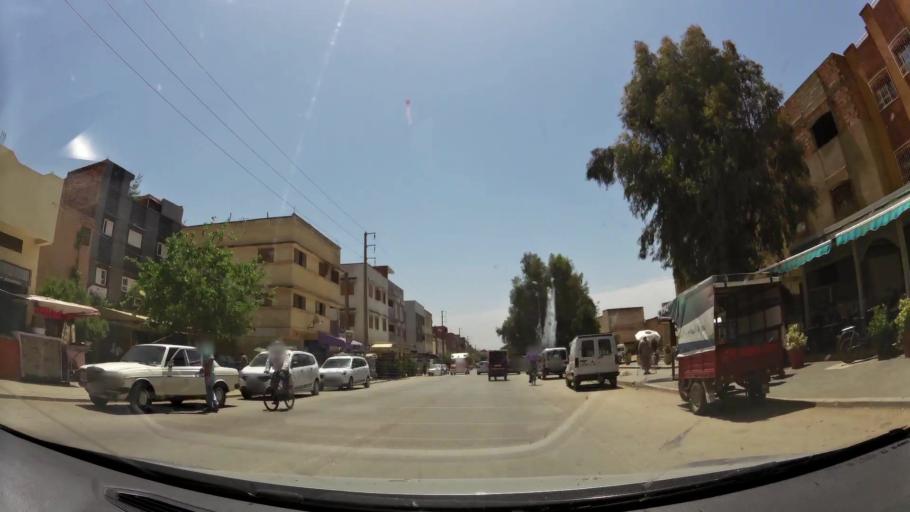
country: MA
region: Rabat-Sale-Zemmour-Zaer
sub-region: Khemisset
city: Khemisset
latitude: 33.8359
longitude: -6.0671
